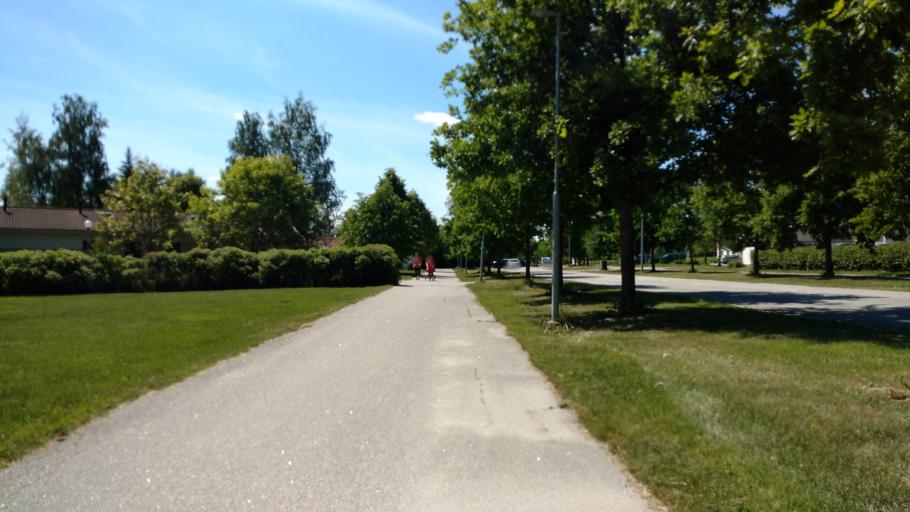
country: FI
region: Varsinais-Suomi
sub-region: Salo
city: Salo
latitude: 60.4027
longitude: 23.1432
